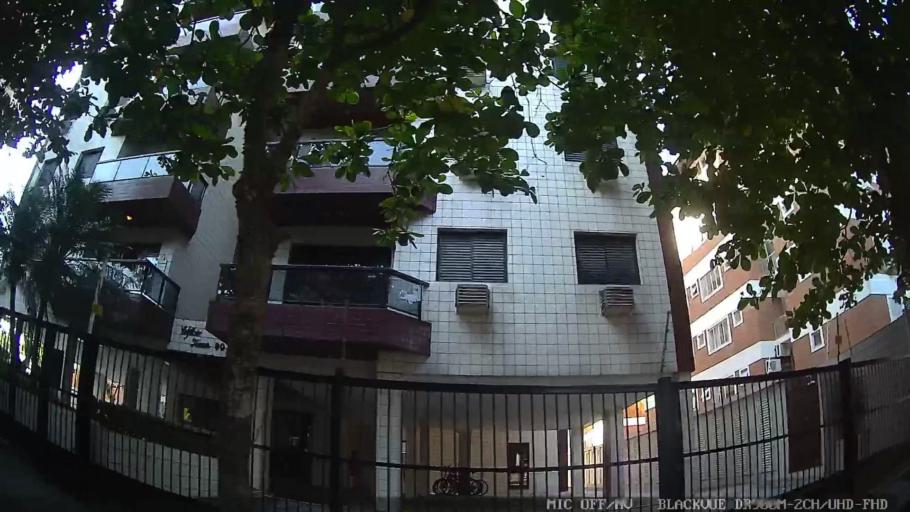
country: BR
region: Sao Paulo
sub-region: Guaruja
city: Guaruja
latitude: -23.9816
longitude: -46.2081
